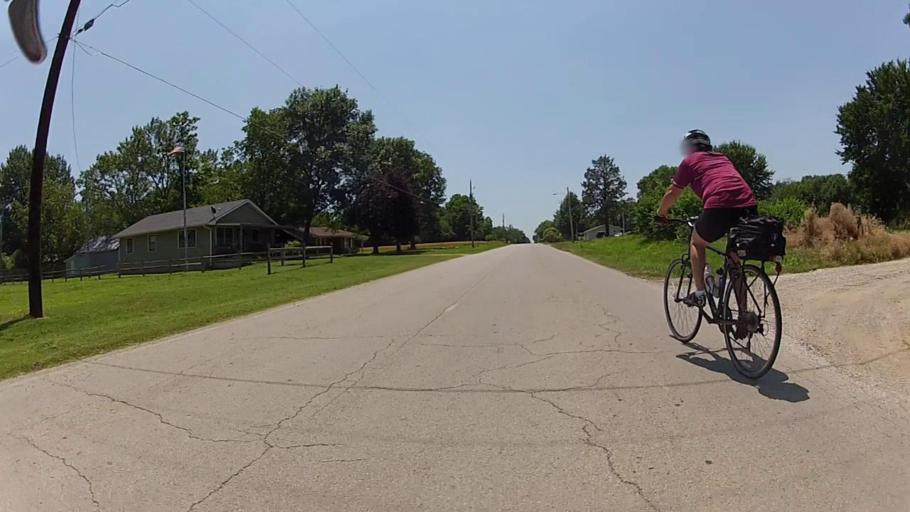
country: US
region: Kansas
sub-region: Montgomery County
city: Cherryvale
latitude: 37.2649
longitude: -95.5370
